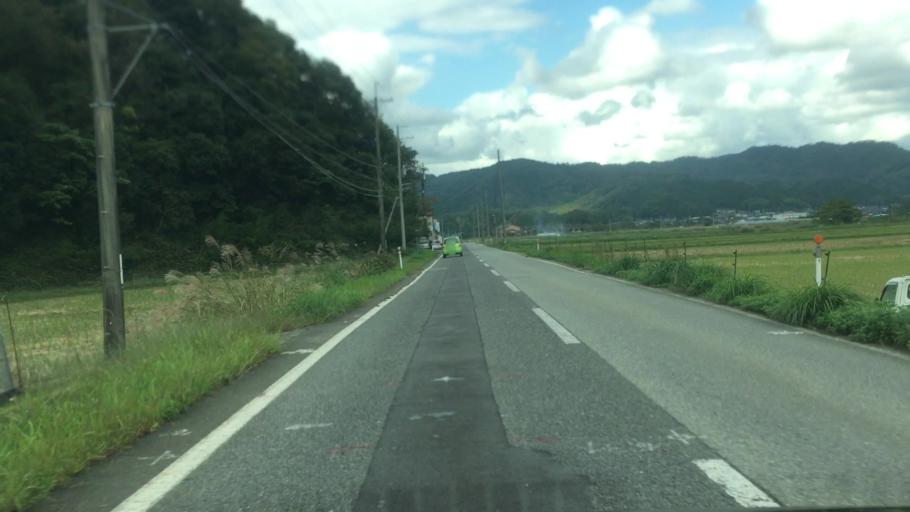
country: JP
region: Hyogo
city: Toyooka
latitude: 35.4456
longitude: 134.7298
